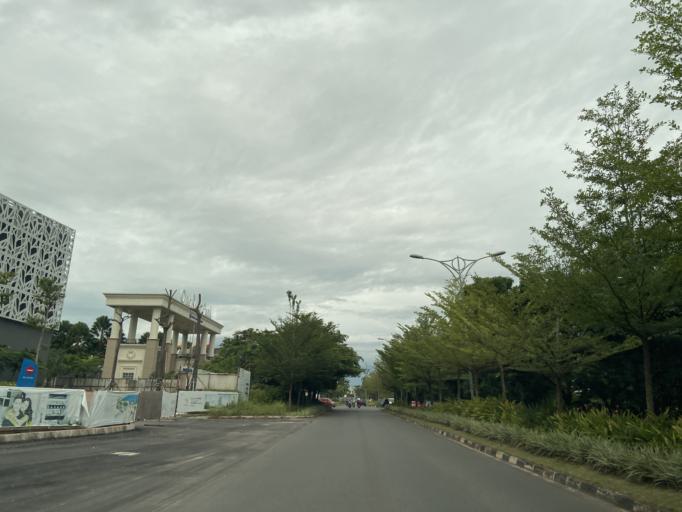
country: SG
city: Singapore
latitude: 1.1136
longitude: 104.0643
